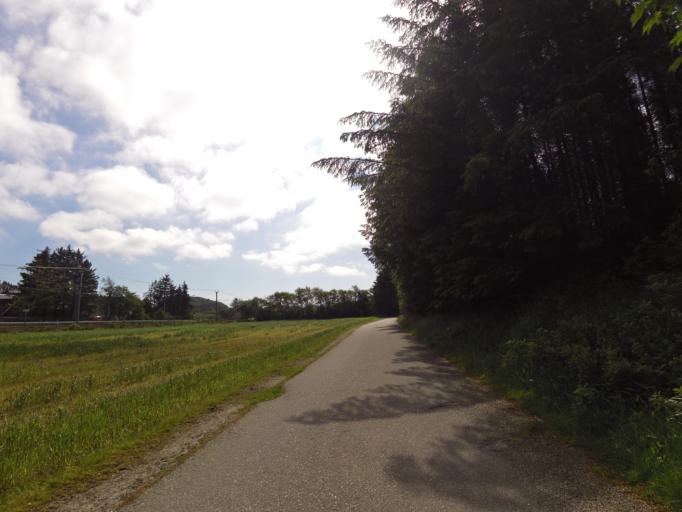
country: NO
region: Rogaland
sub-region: Ha
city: Vigrestad
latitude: 58.5225
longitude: 5.7955
